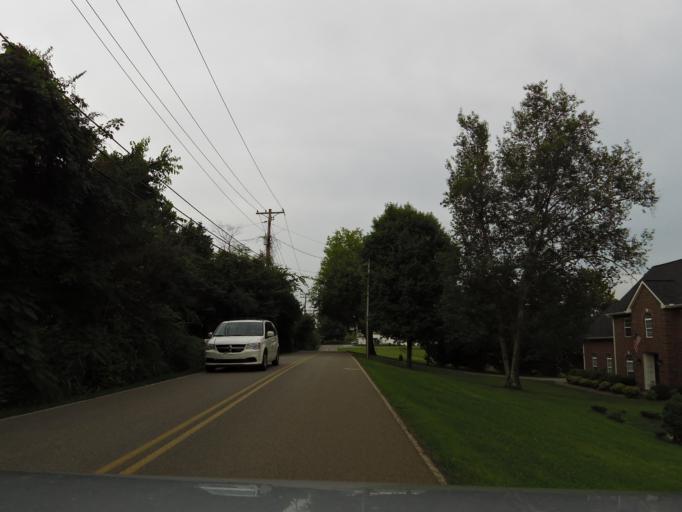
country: US
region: Tennessee
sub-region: Knox County
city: Knoxville
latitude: 35.8858
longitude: -83.9402
